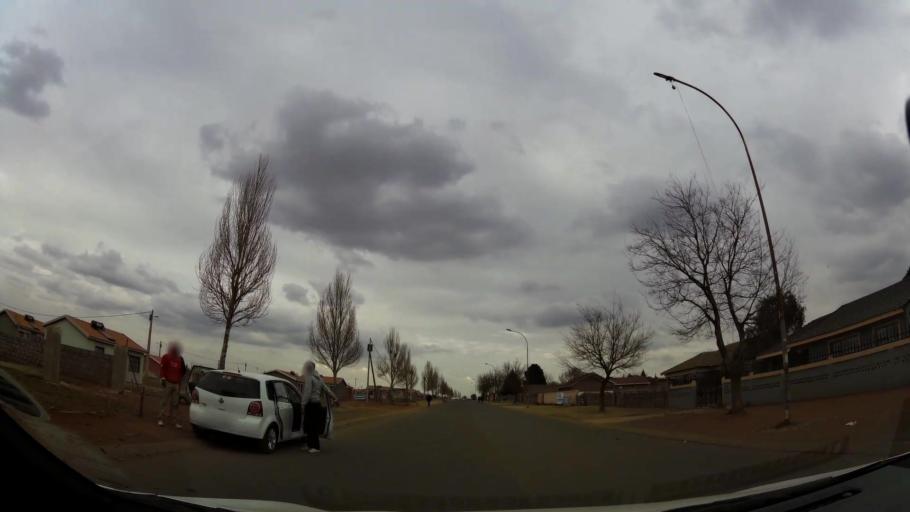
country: ZA
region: Gauteng
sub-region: Ekurhuleni Metropolitan Municipality
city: Germiston
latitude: -26.3936
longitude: 28.1530
